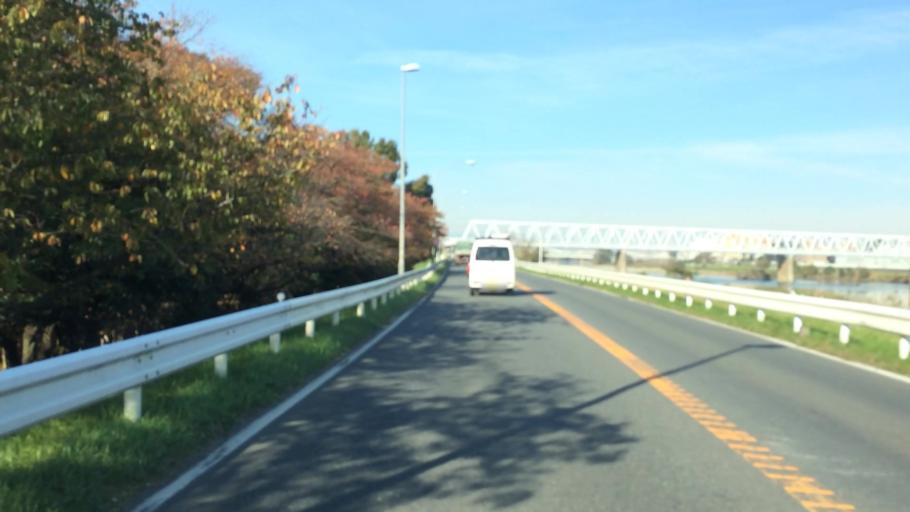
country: JP
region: Tokyo
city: Chofugaoka
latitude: 35.6379
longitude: 139.5380
